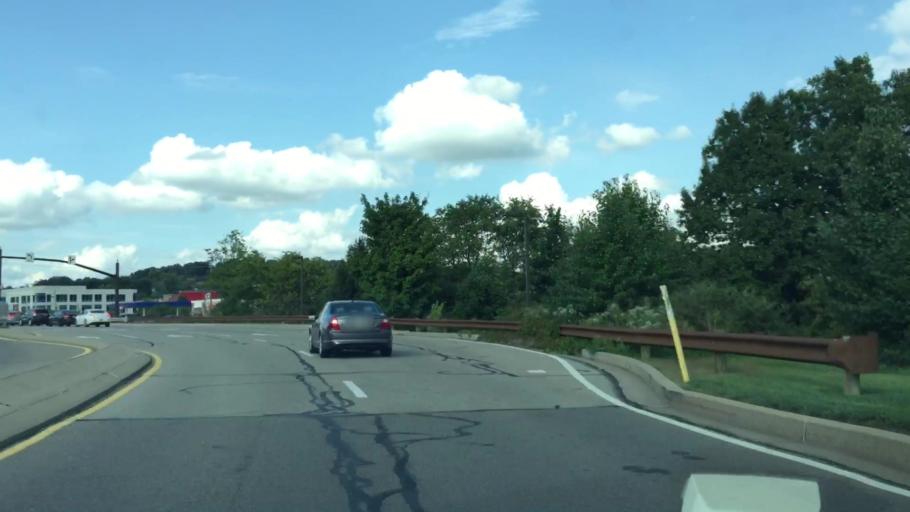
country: US
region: Pennsylvania
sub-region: Butler County
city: Fox Run
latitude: 40.6842
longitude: -80.0879
